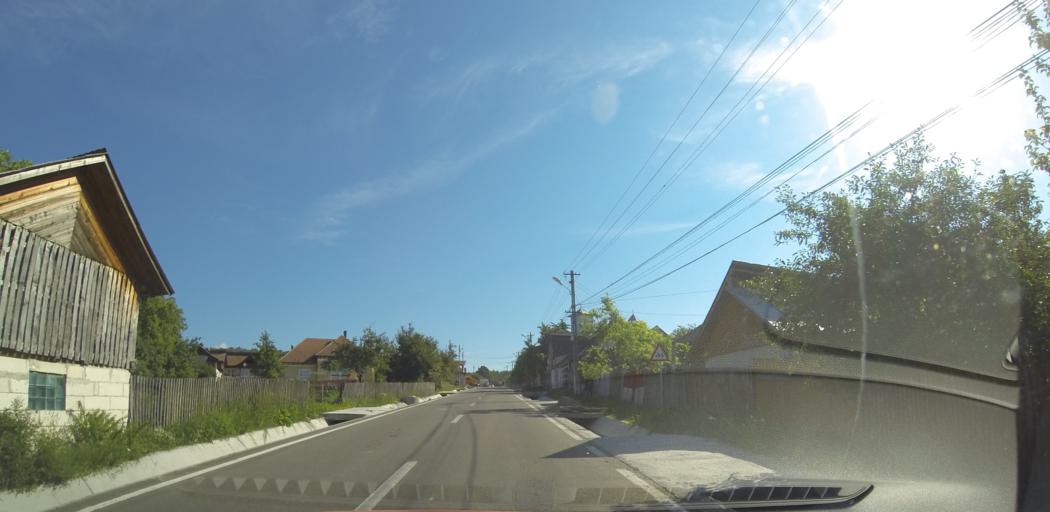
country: RO
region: Valcea
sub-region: Comuna Vaideeni
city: Vaideeni
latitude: 45.1660
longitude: 23.8985
